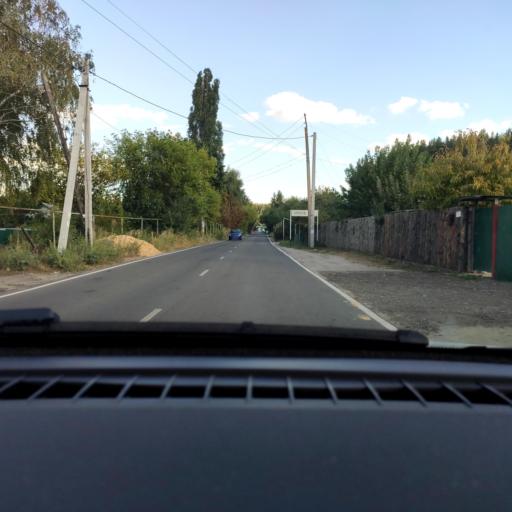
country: RU
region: Voronezj
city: Devitsa
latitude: 51.6571
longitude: 38.9764
